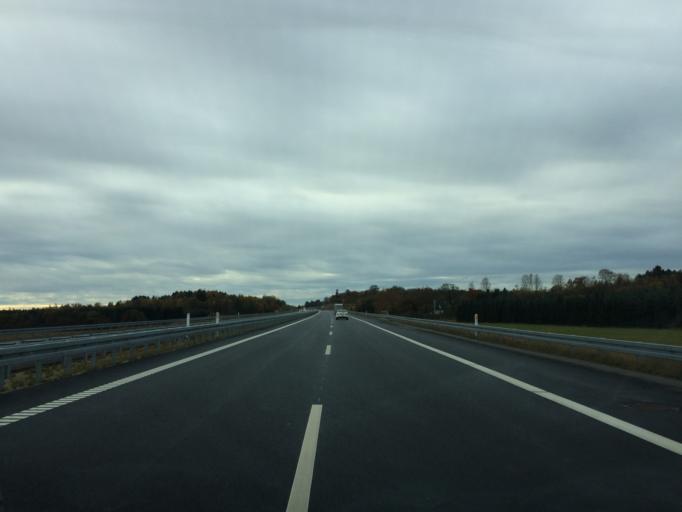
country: DK
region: Central Jutland
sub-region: Silkeborg Kommune
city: Silkeborg
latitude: 56.1844
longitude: 9.4876
